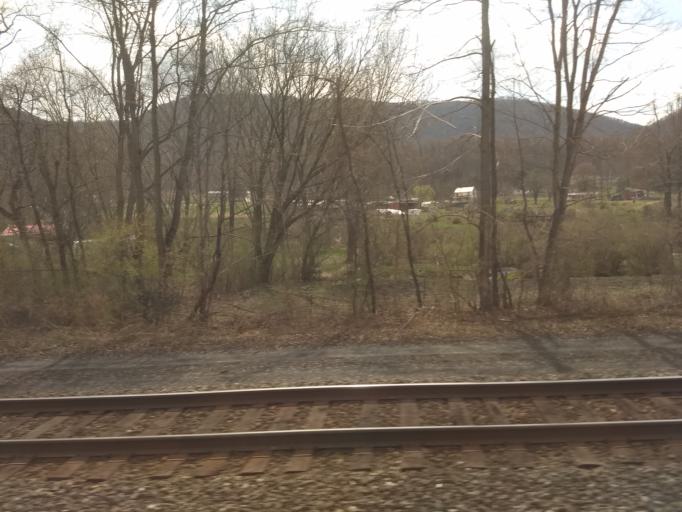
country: US
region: Pennsylvania
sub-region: Huntingdon County
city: Mount Union
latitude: 40.4499
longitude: -77.7456
